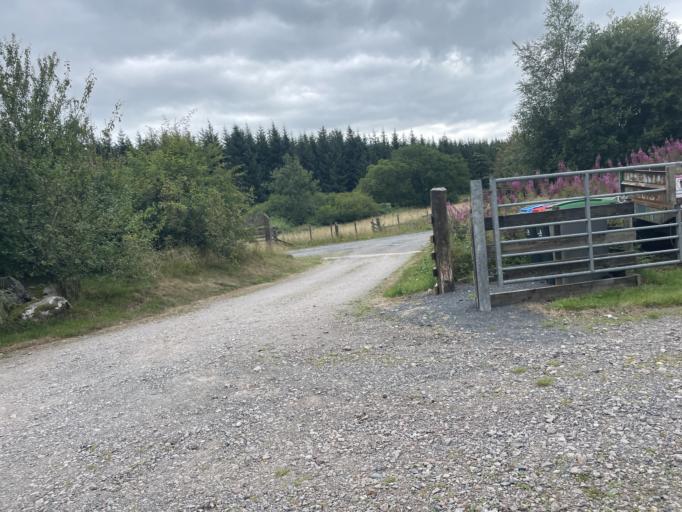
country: GB
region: Scotland
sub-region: Dumfries and Galloway
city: Newton Stewart
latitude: 54.9477
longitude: -4.2582
